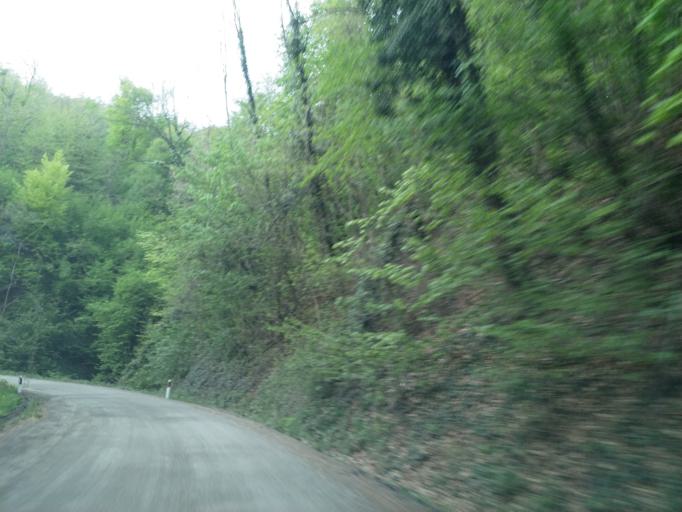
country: RS
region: Central Serbia
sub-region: Pomoravski Okrug
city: Despotovac
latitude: 43.9658
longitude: 21.5598
